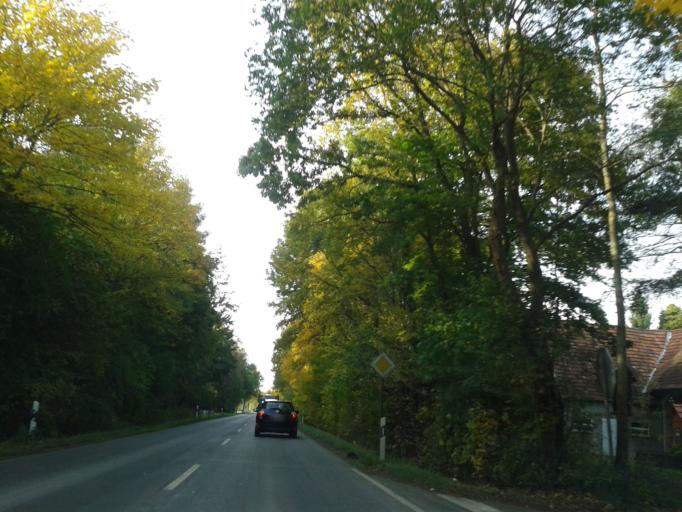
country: DE
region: North Rhine-Westphalia
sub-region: Regierungsbezirk Detmold
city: Salzkotten
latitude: 51.7083
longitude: 8.6664
